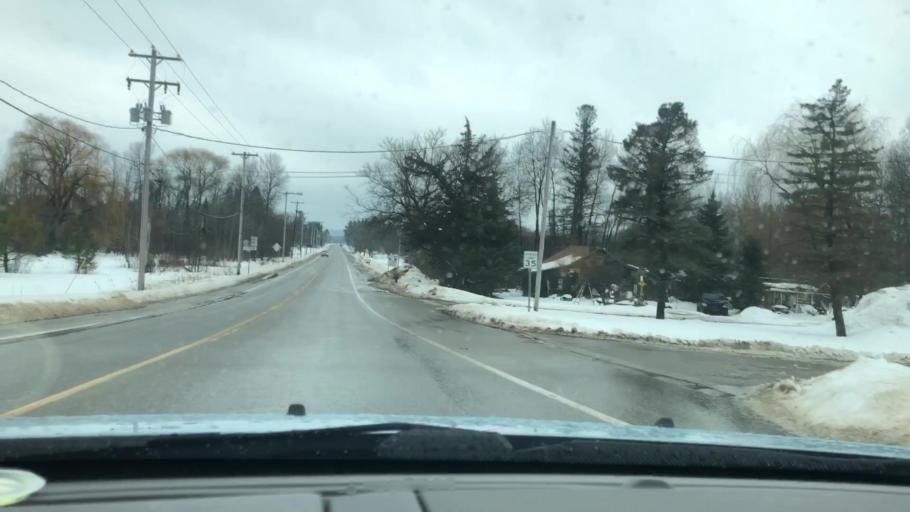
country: US
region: Michigan
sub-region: Charlevoix County
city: East Jordan
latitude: 45.1519
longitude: -85.1191
